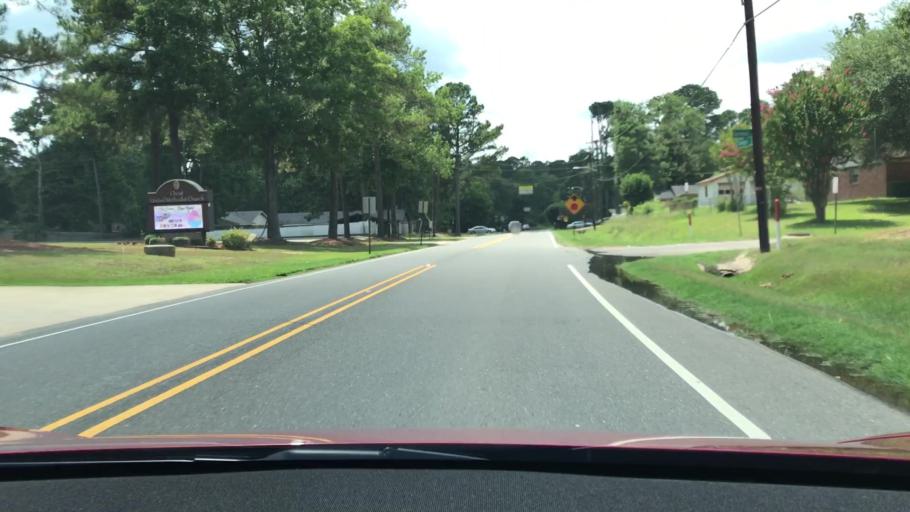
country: US
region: Louisiana
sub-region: De Soto Parish
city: Stonewall
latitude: 32.3891
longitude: -93.7881
